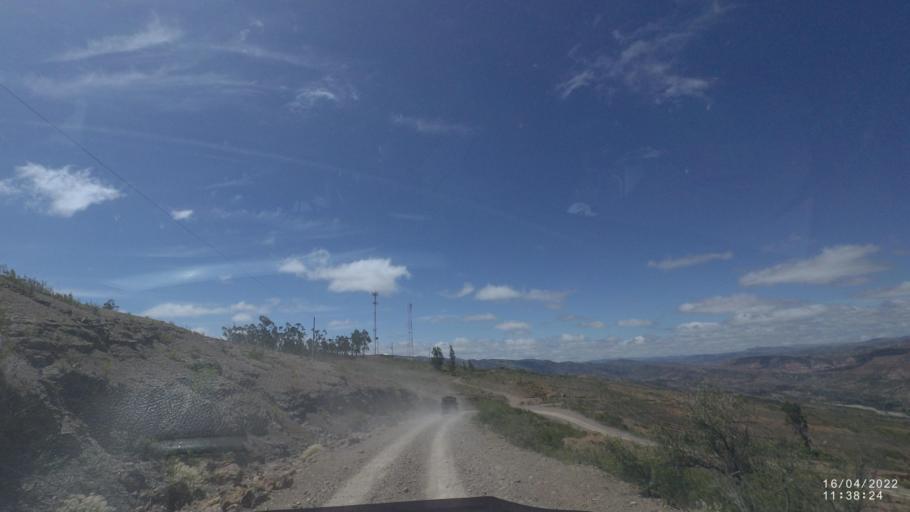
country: BO
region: Cochabamba
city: Mizque
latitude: -17.9640
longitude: -65.6382
